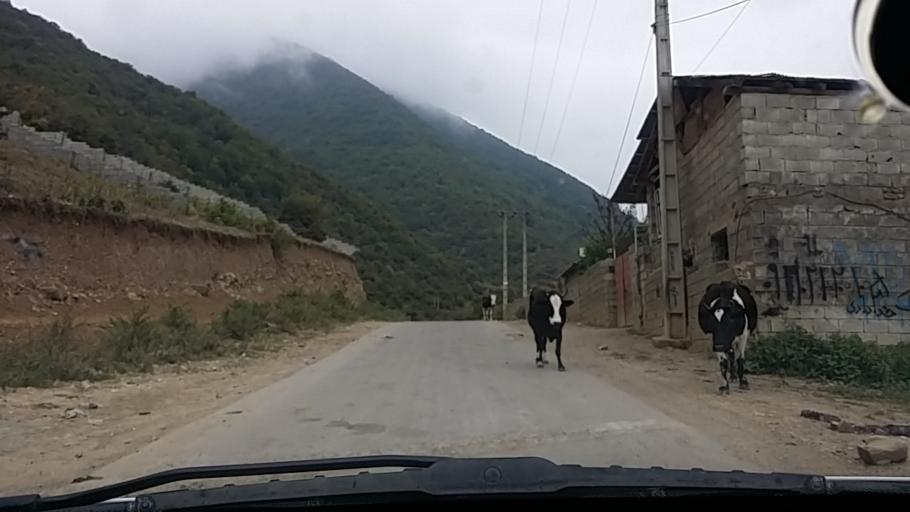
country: IR
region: Mazandaran
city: `Abbasabad
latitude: 36.4689
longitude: 51.1397
